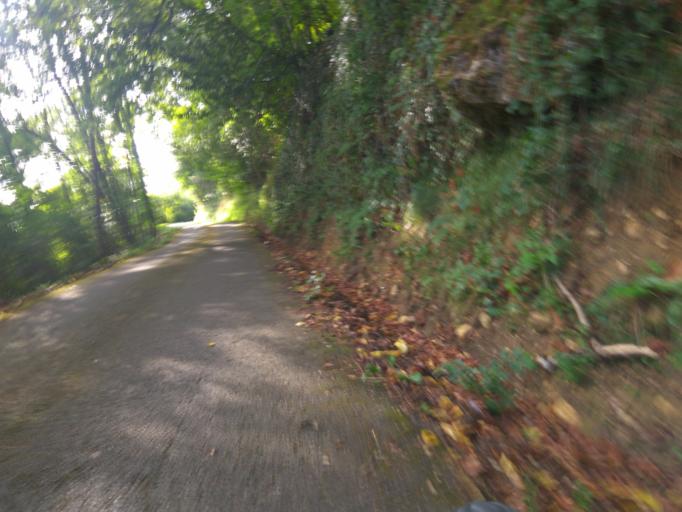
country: FR
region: Aquitaine
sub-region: Departement des Pyrenees-Atlantiques
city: Mazeres-Lezons
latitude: 43.2670
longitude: -0.3464
